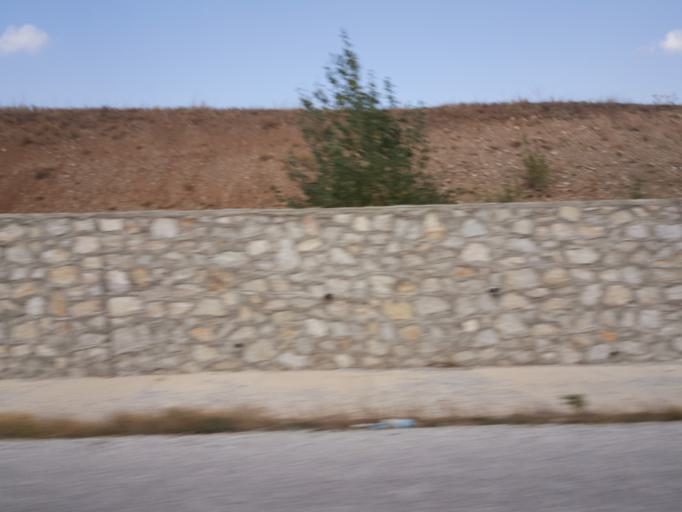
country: TR
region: Corum
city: Alaca
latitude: 40.1548
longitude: 34.7299
